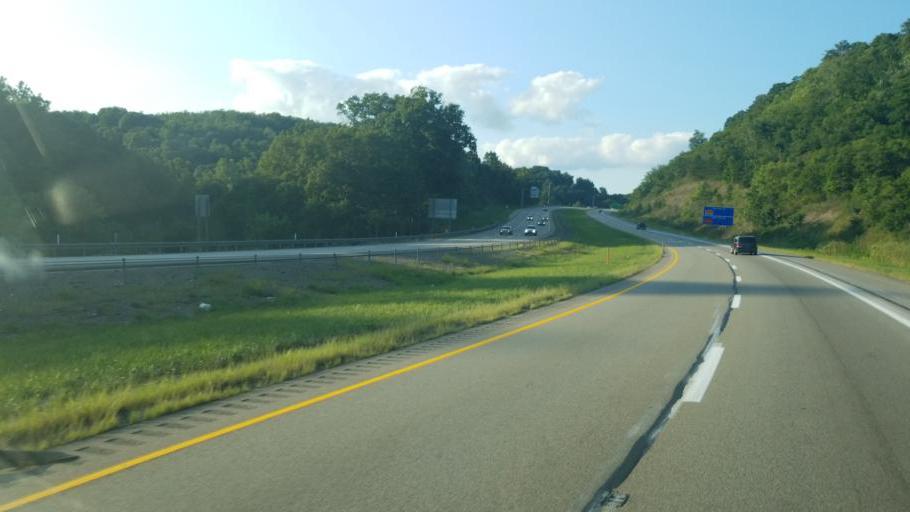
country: US
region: Pennsylvania
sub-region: Allegheny County
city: Emsworth
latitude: 40.5413
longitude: -80.1217
